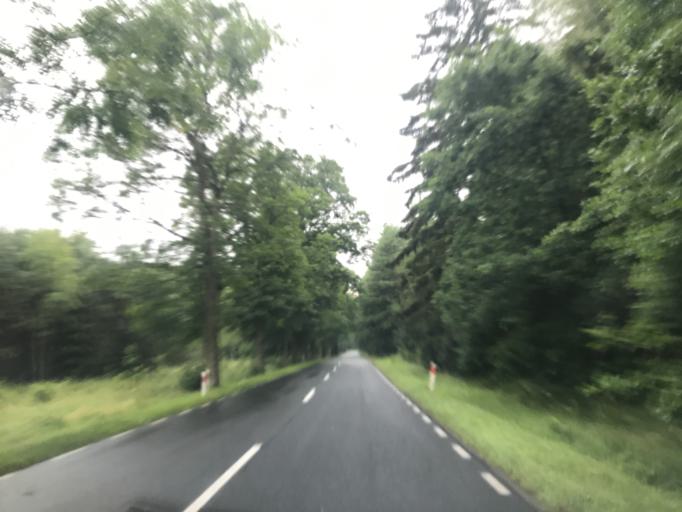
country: PL
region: West Pomeranian Voivodeship
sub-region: Powiat szczecinecki
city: Grzmiaca
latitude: 53.9756
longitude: 16.4306
